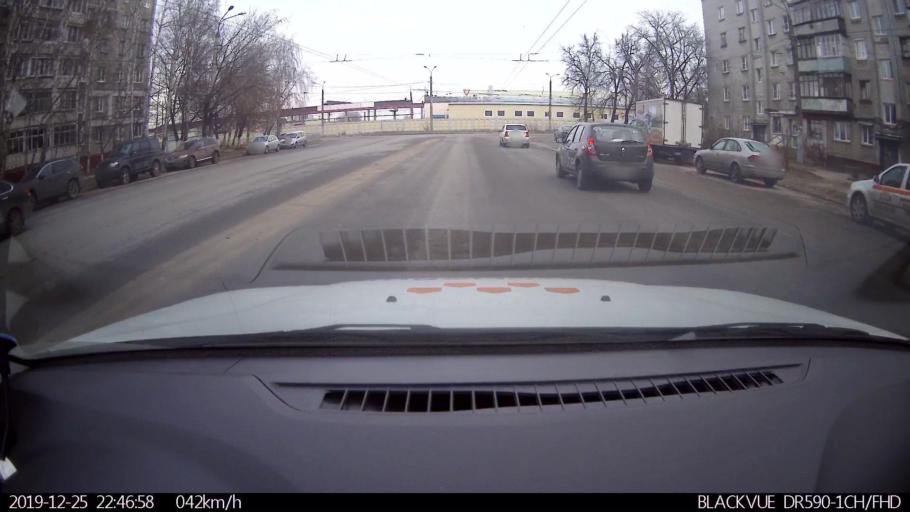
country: RU
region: Nizjnij Novgorod
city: Burevestnik
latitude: 56.2385
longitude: 43.8697
